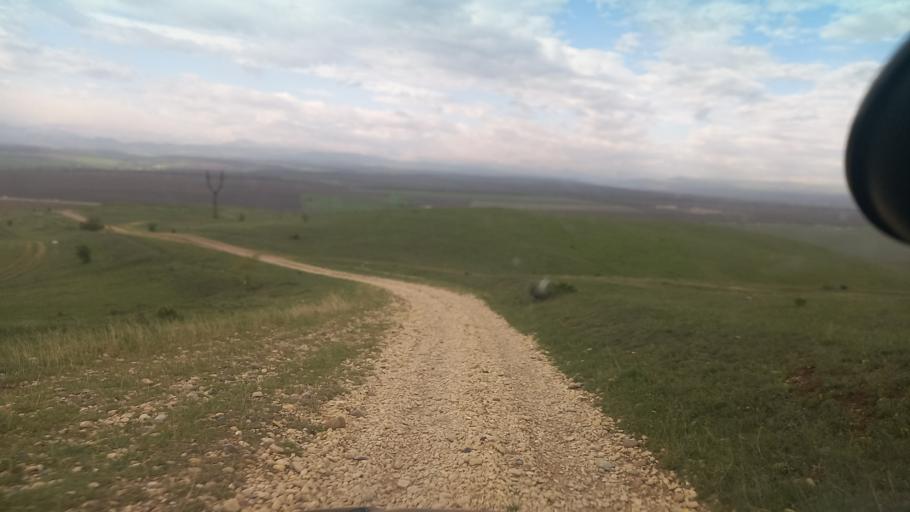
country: RU
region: Kabardino-Balkariya
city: Kuba-Taba
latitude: 43.8046
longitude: 43.4005
